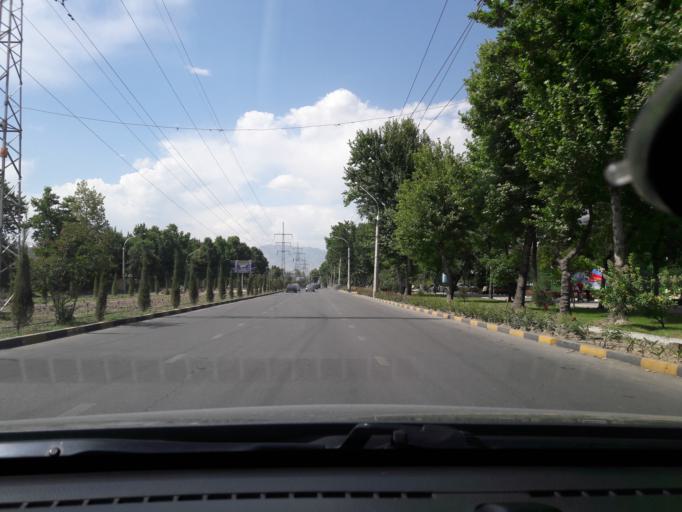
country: TJ
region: Dushanbe
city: Dushanbe
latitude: 38.5416
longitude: 68.7622
